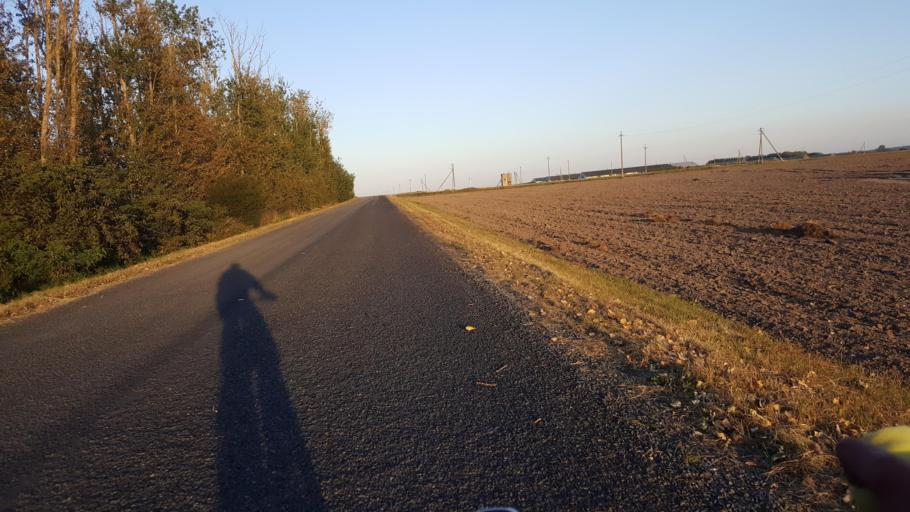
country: BY
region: Brest
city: Vysokaye
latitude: 52.2961
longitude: 23.5300
